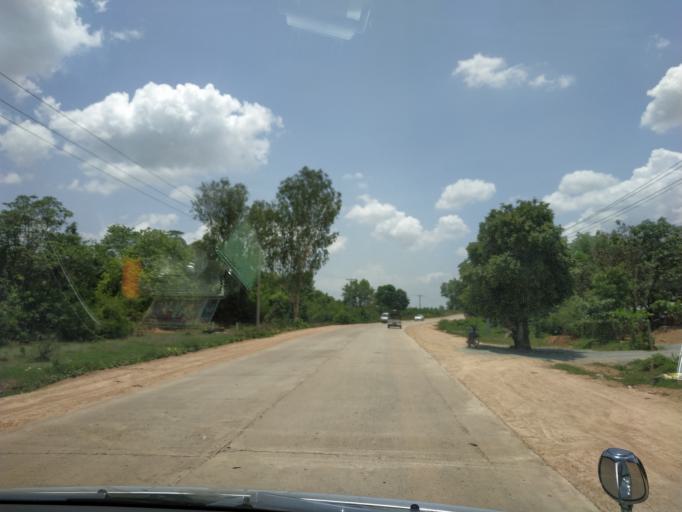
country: MM
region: Bago
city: Bago
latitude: 17.4736
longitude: 96.4734
